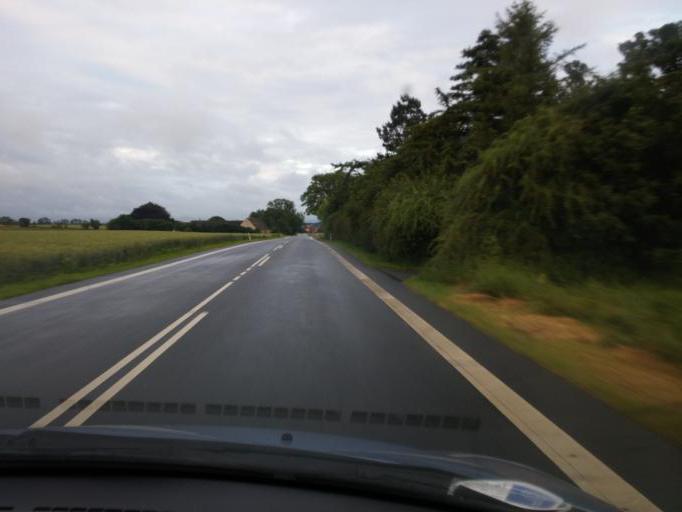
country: DK
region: South Denmark
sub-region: Kerteminde Kommune
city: Kerteminde
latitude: 55.4866
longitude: 10.6589
